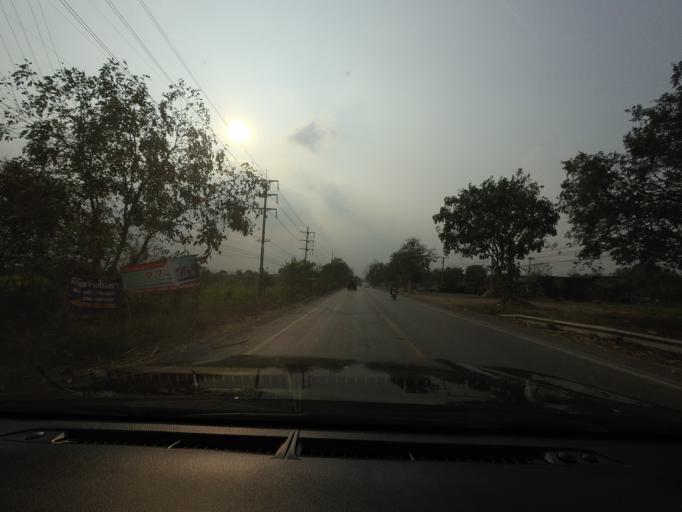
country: TH
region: Sara Buri
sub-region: Amphoe Wang Muang
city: Wang Muang
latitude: 14.8415
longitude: 101.0906
